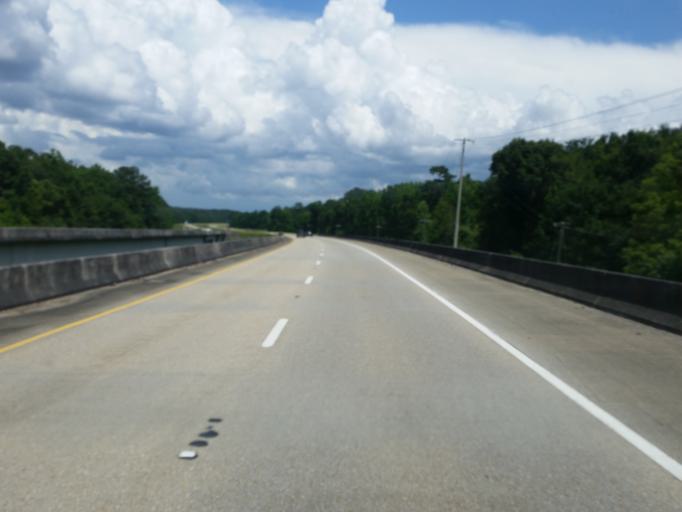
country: US
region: Mississippi
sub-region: Perry County
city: New Augusta
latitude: 31.1074
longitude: -88.8076
